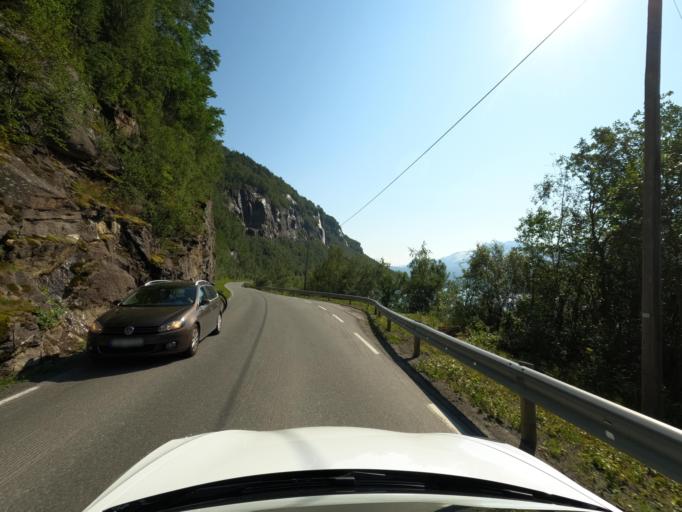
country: NO
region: Nordland
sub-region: Narvik
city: Narvik
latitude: 68.3527
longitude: 17.2757
